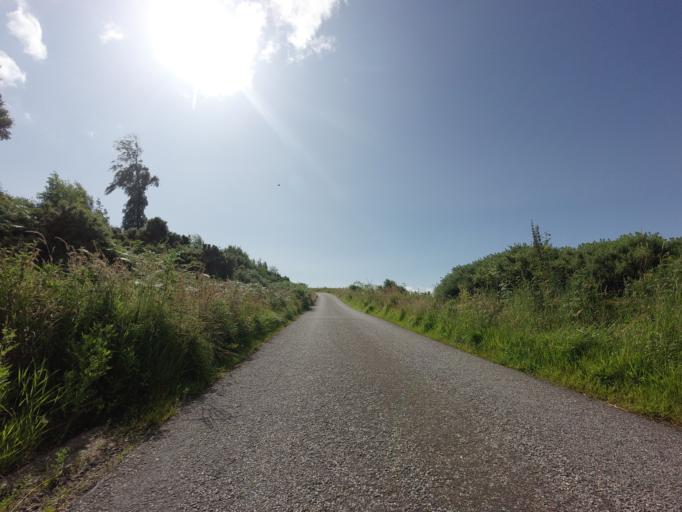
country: GB
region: Scotland
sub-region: Highland
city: Nairn
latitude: 57.5323
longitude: -3.8644
